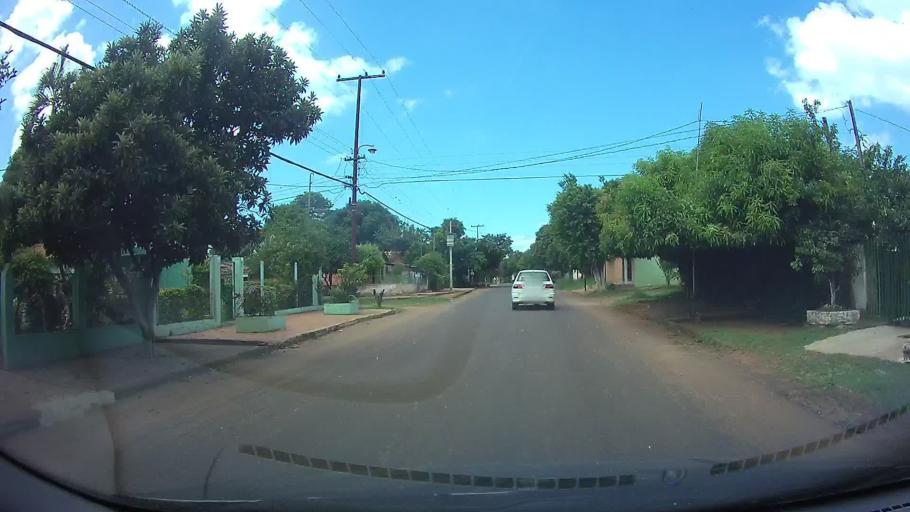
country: PY
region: Central
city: Itaugua
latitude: -25.3882
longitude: -57.3483
